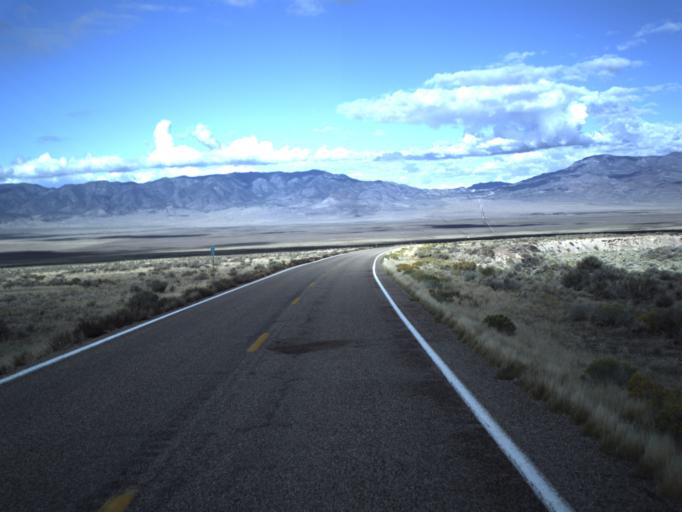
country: US
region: Utah
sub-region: Beaver County
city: Milford
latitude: 38.4367
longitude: -113.3065
